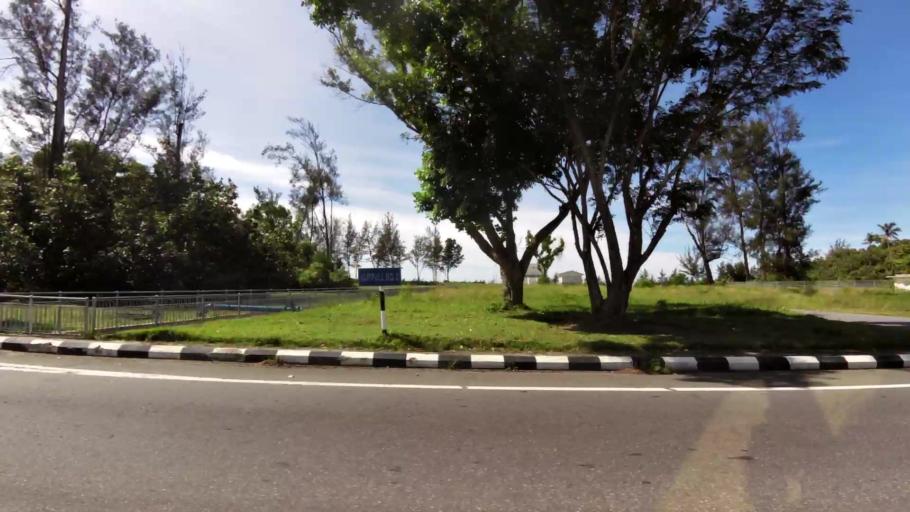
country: BN
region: Belait
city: Kuala Belait
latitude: 4.5885
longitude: 114.2029
